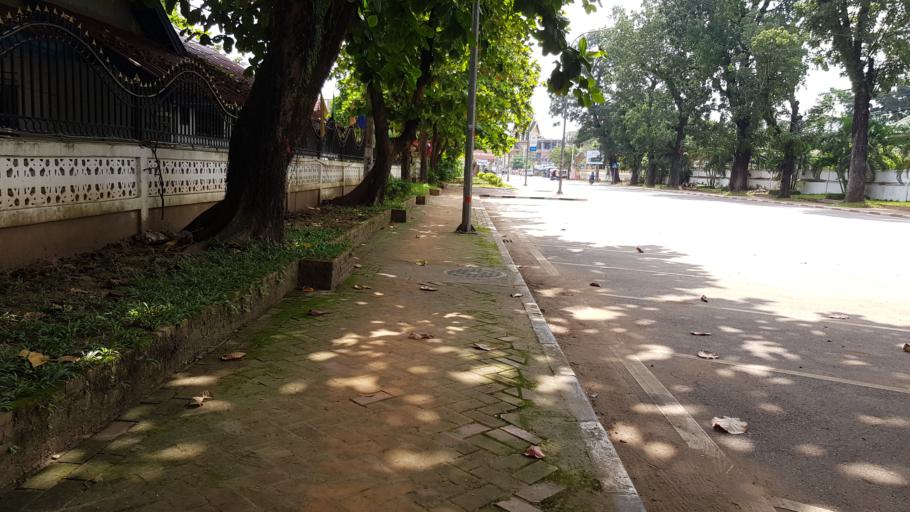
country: LA
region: Vientiane
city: Vientiane
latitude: 17.9604
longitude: 102.6137
